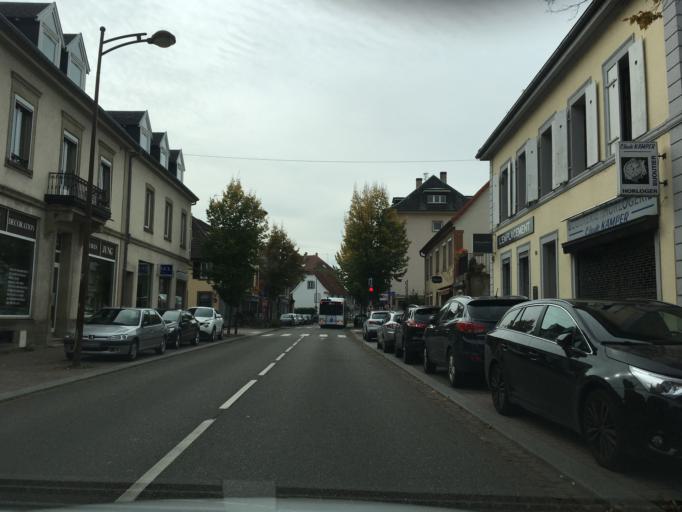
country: FR
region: Alsace
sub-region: Departement du Bas-Rhin
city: Bischheim
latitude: 48.6014
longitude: 7.7821
